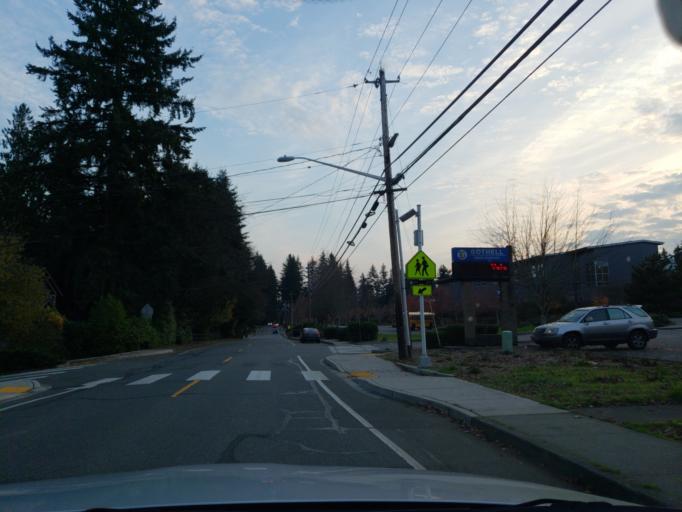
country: US
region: Washington
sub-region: King County
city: Bothell
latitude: 47.7609
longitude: -122.2177
